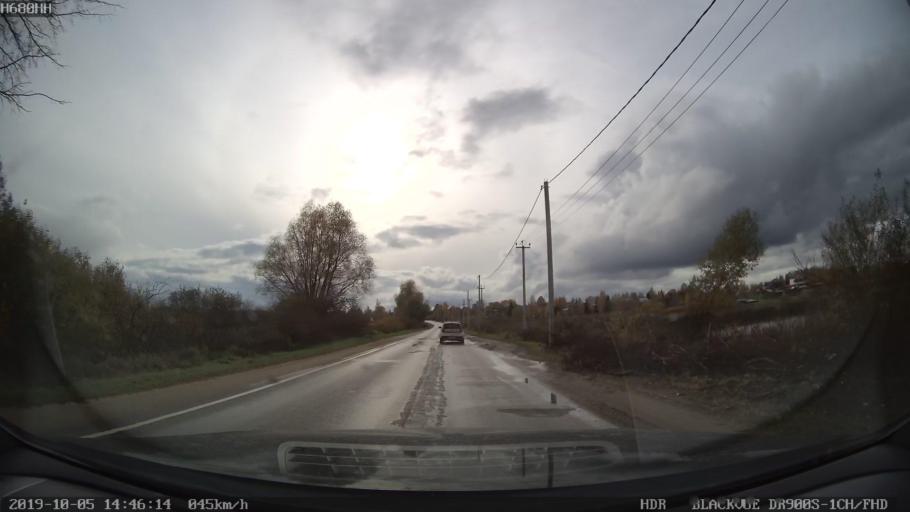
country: RU
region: Moskovskaya
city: Solnechnogorsk
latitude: 56.2275
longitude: 36.9106
